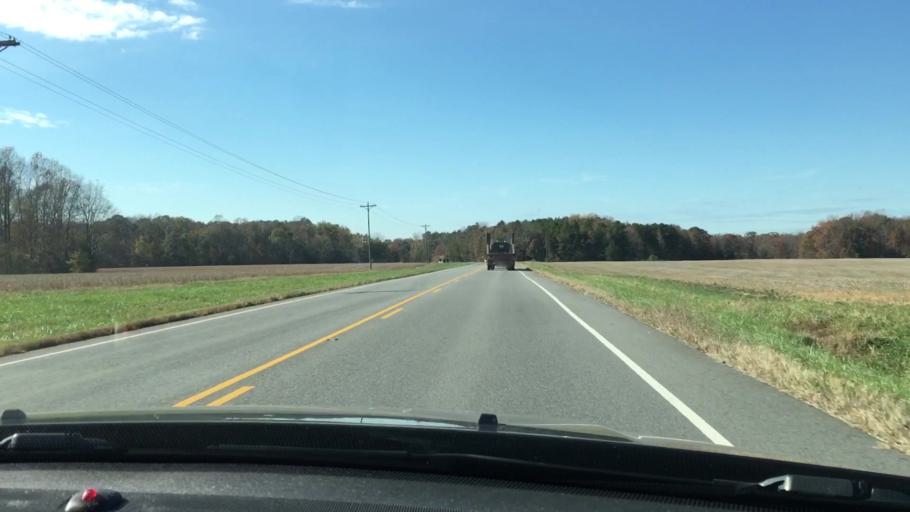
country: US
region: Virginia
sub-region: Hanover County
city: Hanover
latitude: 37.8108
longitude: -77.2775
